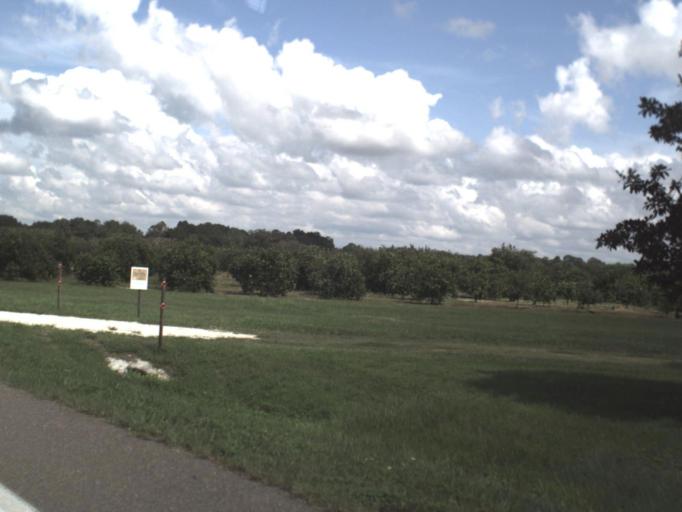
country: US
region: Florida
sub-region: Hardee County
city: Wauchula
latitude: 27.4736
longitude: -82.0549
